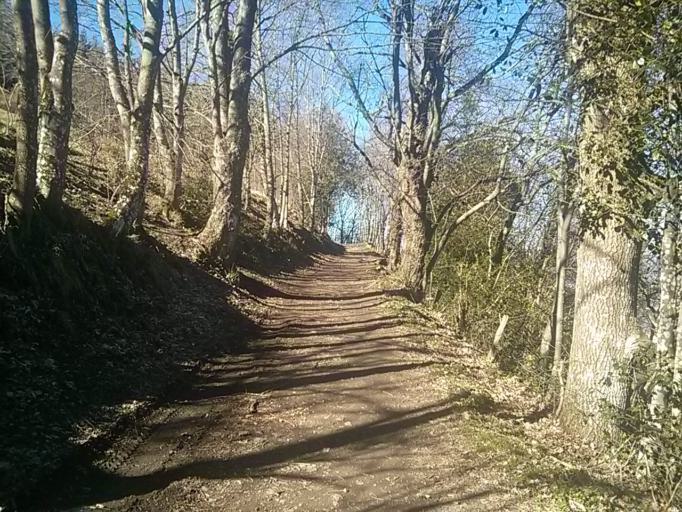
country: FR
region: Rhone-Alpes
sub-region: Departement de la Loire
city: Saint-Jean-Bonnefonds
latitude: 45.4151
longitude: 4.4415
